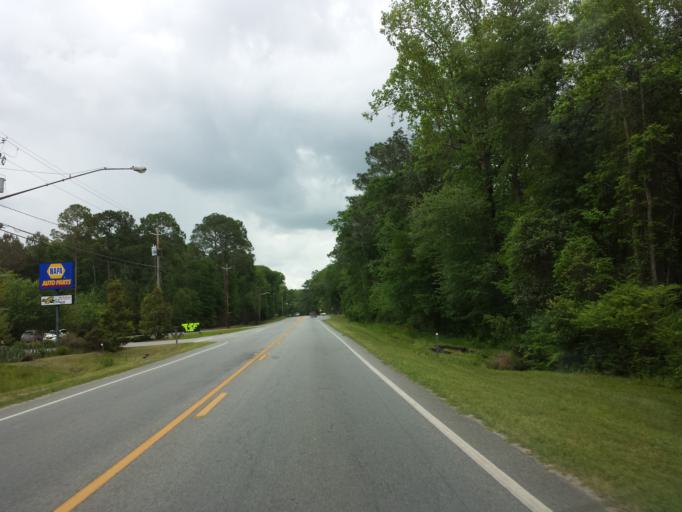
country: US
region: Georgia
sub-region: Lowndes County
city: Hahira
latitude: 30.9914
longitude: -83.3847
